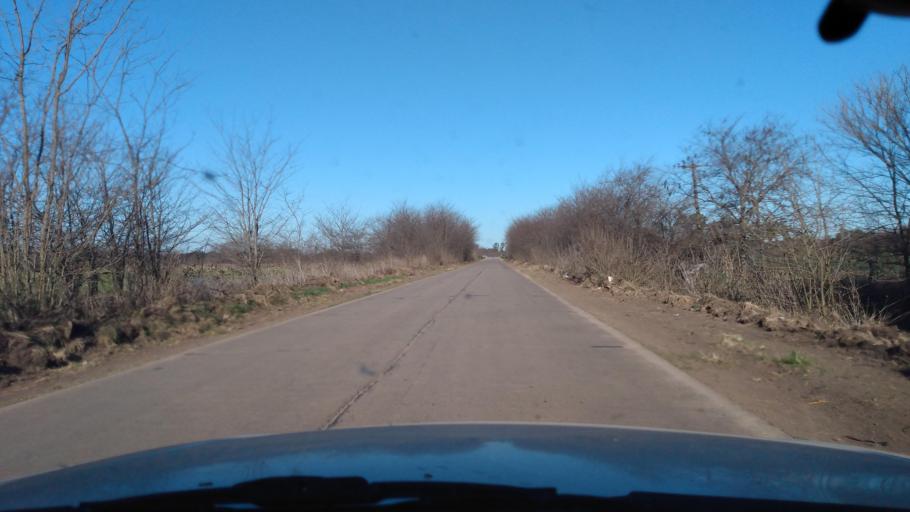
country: AR
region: Buenos Aires
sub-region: Partido de Lujan
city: Lujan
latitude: -34.6156
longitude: -59.2639
